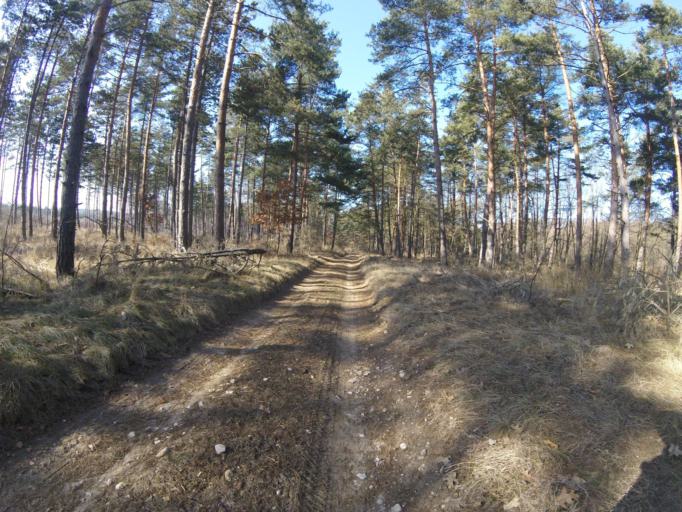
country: HU
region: Komarom-Esztergom
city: Oroszlany
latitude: 47.4567
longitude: 18.3659
